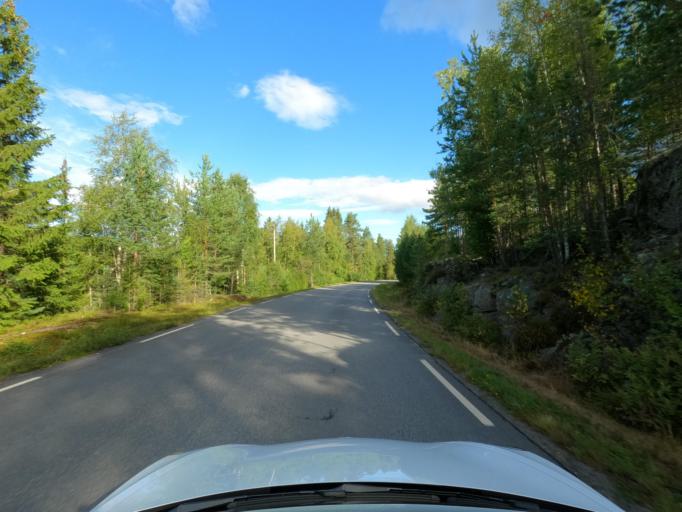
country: NO
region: Telemark
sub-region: Hjartdal
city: Sauland
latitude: 59.7898
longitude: 9.1023
